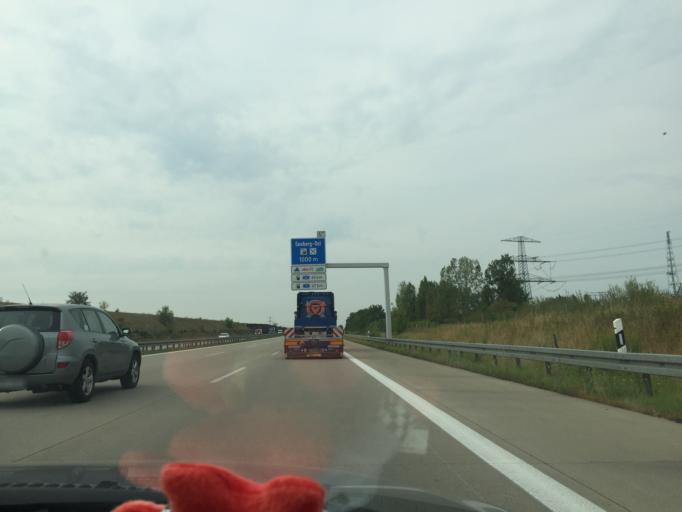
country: DE
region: Brandenburg
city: Neuenhagen
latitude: 52.5326
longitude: 13.7061
